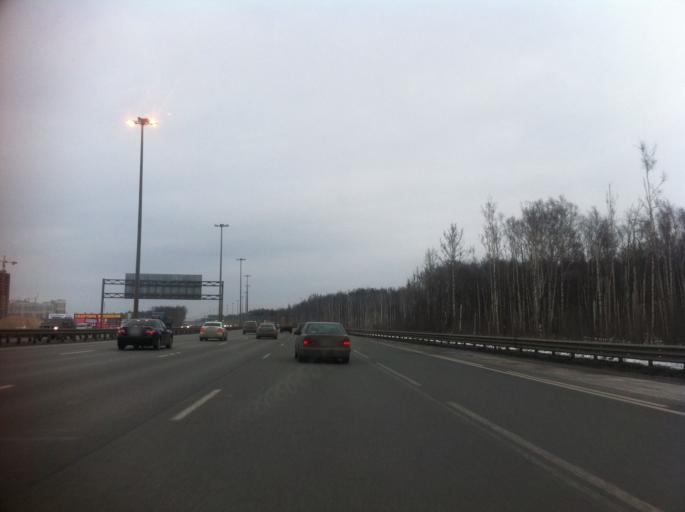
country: RU
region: Leningrad
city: Rybatskoye
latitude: 59.8898
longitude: 30.5244
